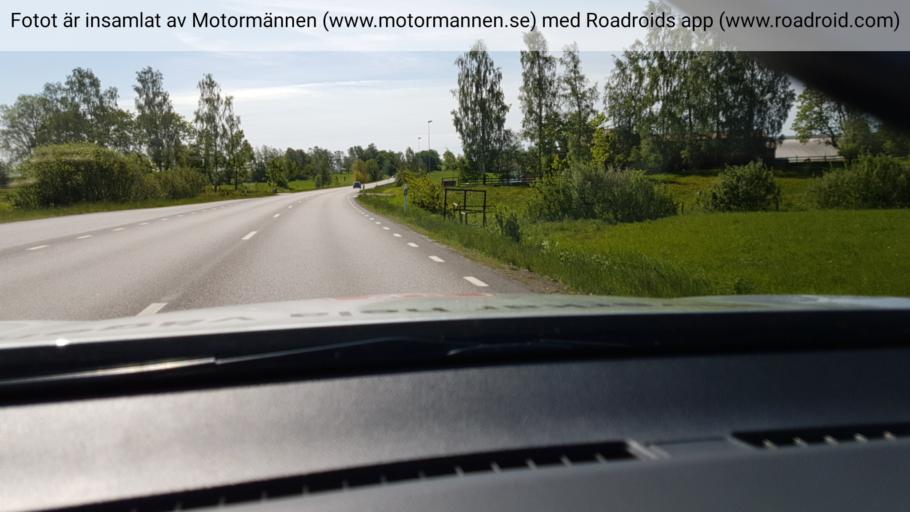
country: SE
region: Vaestra Goetaland
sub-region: Hjo Kommun
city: Hjo
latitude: 58.3331
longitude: 14.2522
